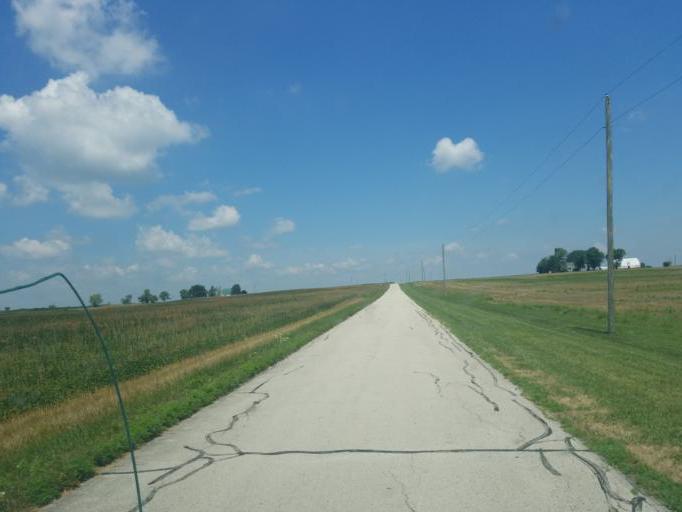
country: US
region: Ohio
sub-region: Allen County
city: Spencerville
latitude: 40.6734
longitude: -84.4350
